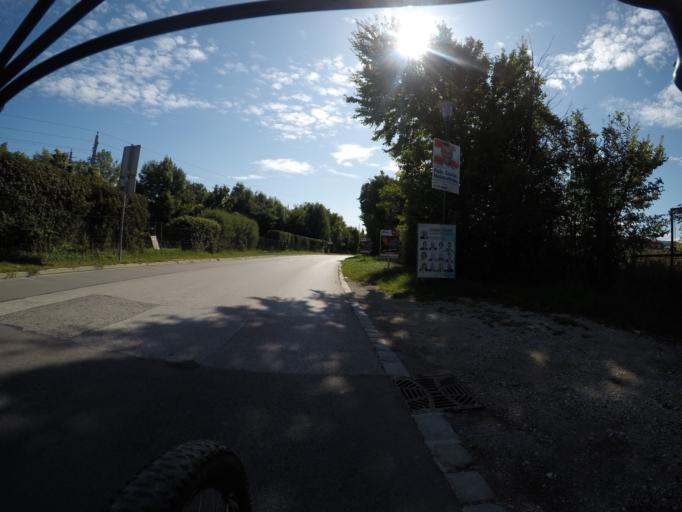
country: AT
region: Lower Austria
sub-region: Politischer Bezirk Modling
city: Maria Enzersdorf
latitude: 48.1023
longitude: 16.2879
